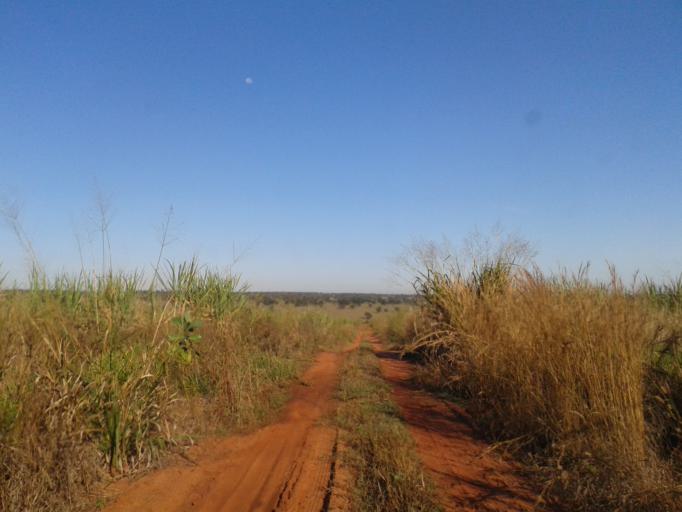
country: BR
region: Minas Gerais
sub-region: Santa Vitoria
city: Santa Vitoria
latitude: -19.0191
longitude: -50.3708
